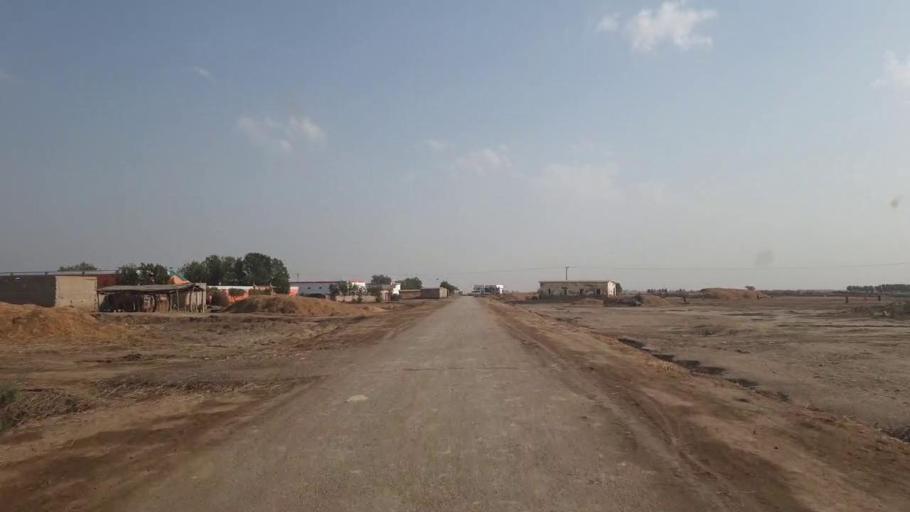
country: PK
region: Sindh
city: Kario
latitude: 24.5817
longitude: 68.5409
